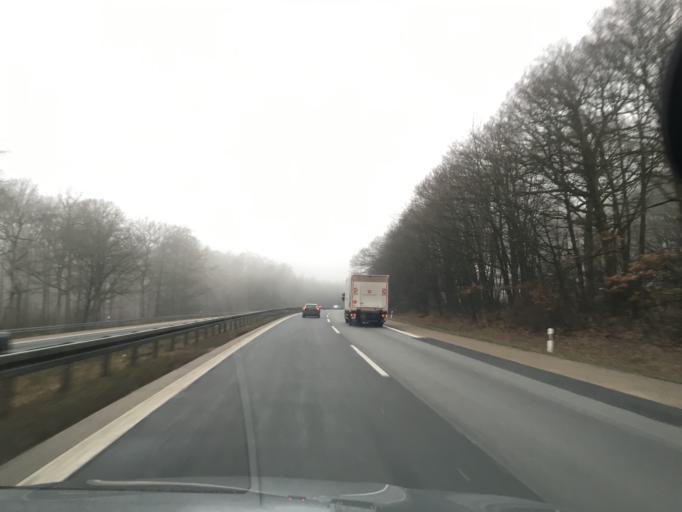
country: DE
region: Bavaria
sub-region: Regierungsbezirk Unterfranken
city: Bischbrunn
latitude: 49.8570
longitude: 9.4893
